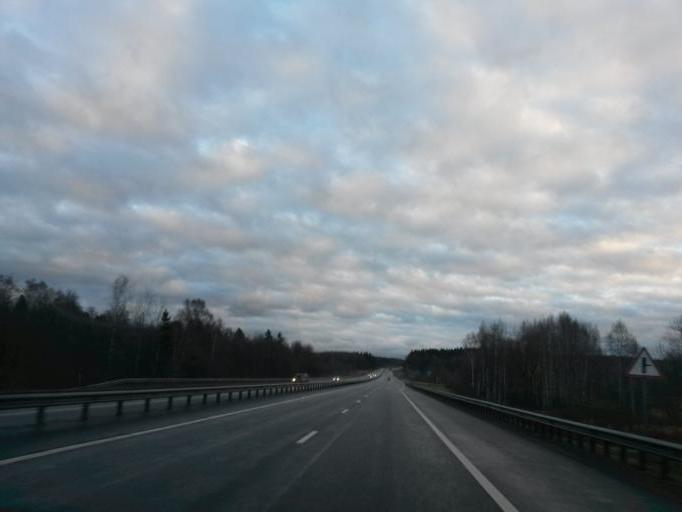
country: RU
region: Moskovskaya
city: Svatkovo
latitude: 56.3553
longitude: 38.2826
